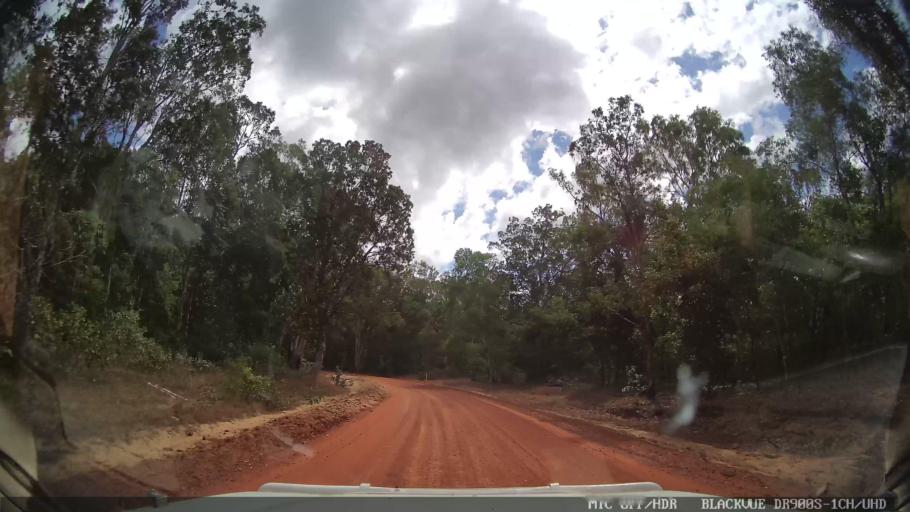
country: AU
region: Queensland
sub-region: Cook
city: Cooktown
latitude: -15.3028
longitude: 144.6143
